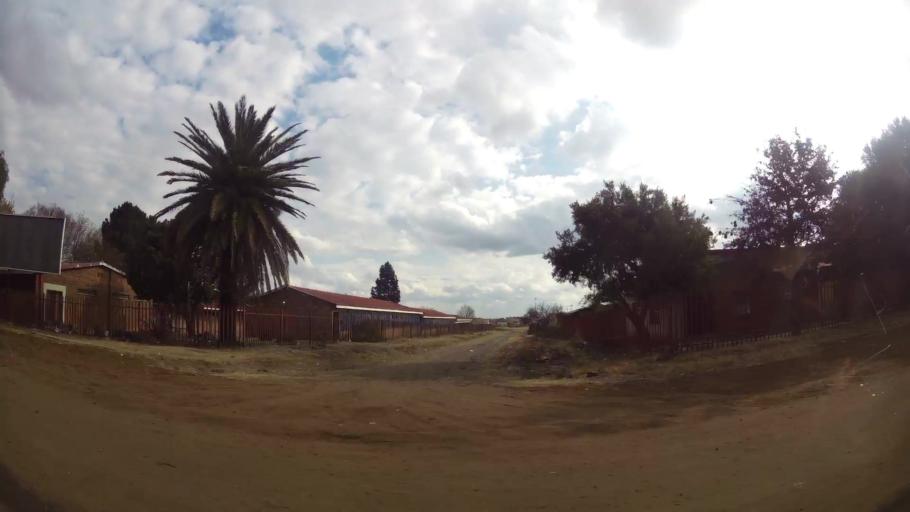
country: ZA
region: Orange Free State
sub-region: Fezile Dabi District Municipality
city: Sasolburg
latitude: -26.8433
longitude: 27.8461
